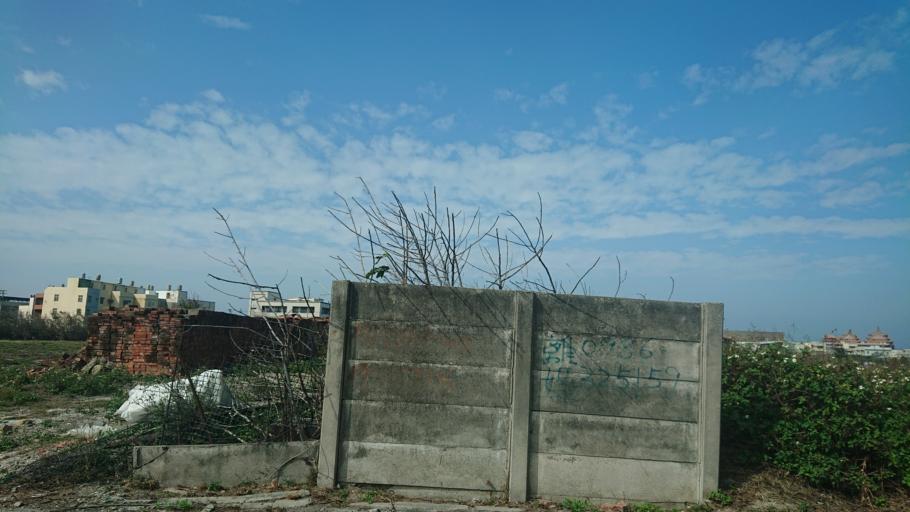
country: TW
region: Taiwan
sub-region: Changhua
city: Chang-hua
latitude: 23.9248
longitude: 120.3227
